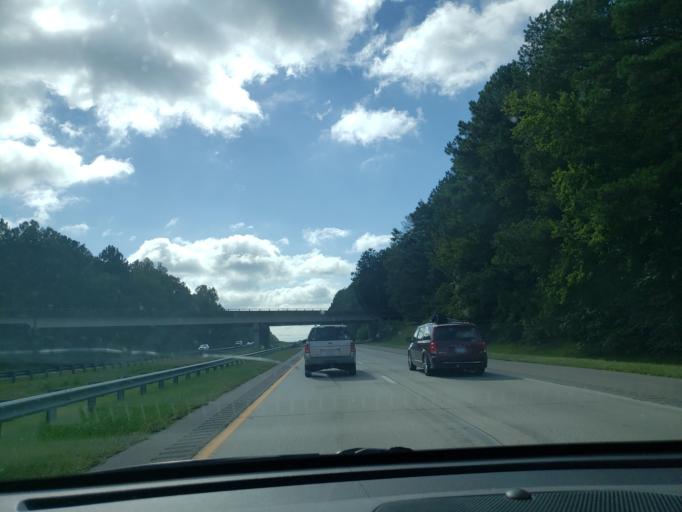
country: US
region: North Carolina
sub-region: Granville County
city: Oxford
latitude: 36.3156
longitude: -78.5420
